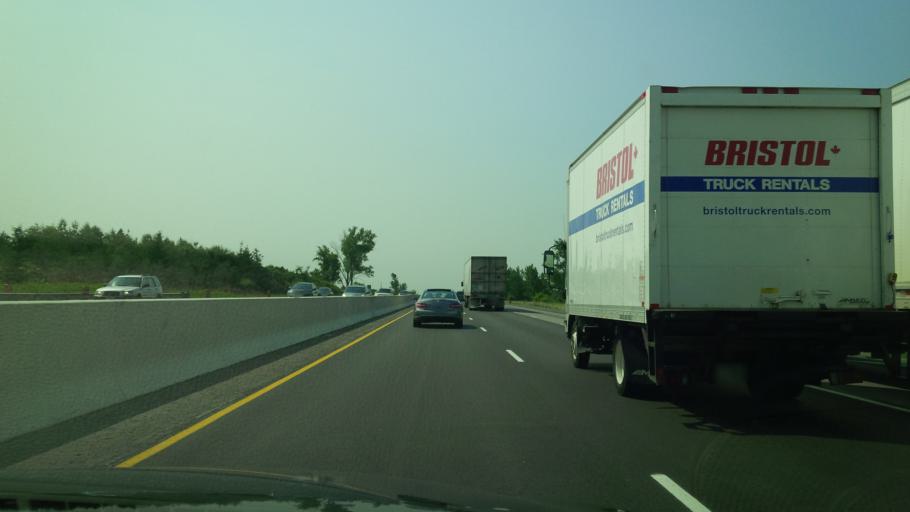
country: CA
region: Ontario
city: Bradford West Gwillimbury
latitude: 44.1411
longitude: -79.6411
